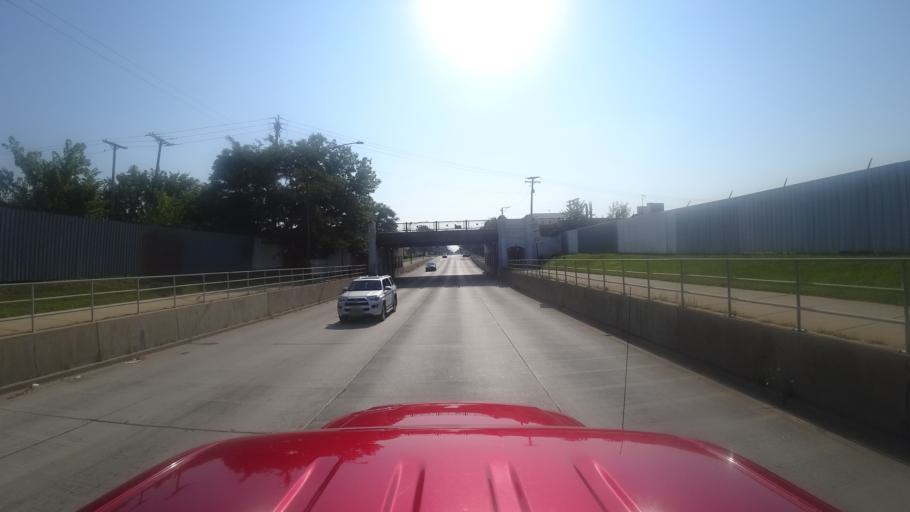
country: US
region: Illinois
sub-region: Cook County
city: Cicero
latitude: 41.8077
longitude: -87.7390
